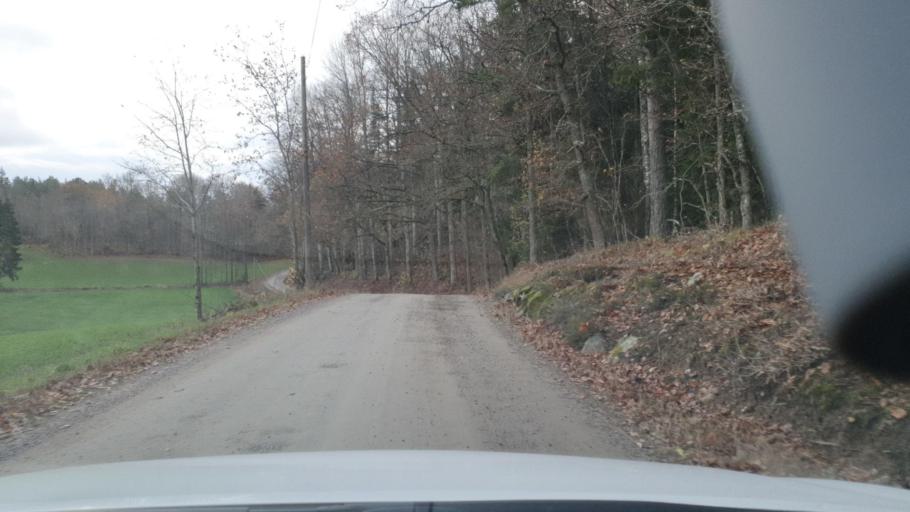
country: SE
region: Kalmar
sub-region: Vasterviks Kommun
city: Ankarsrum
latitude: 57.7023
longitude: 16.4545
